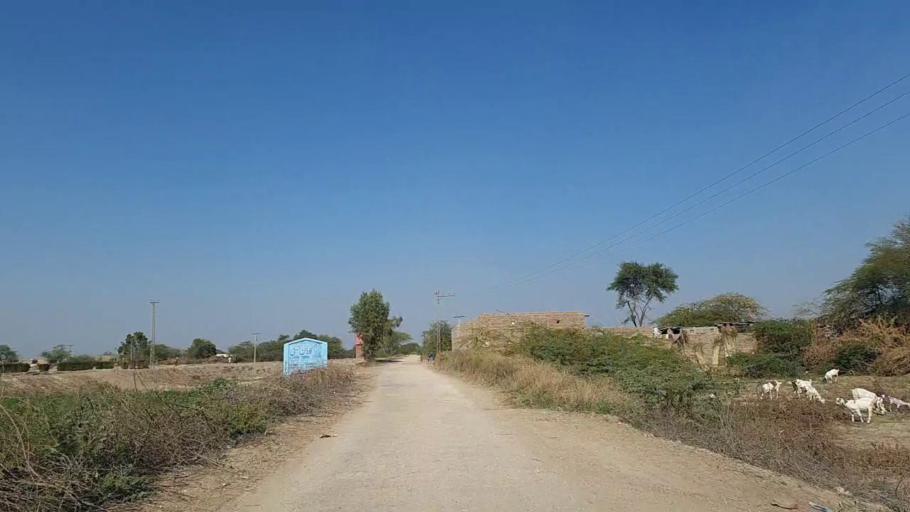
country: PK
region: Sindh
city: Nawabshah
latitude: 26.2530
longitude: 68.4411
